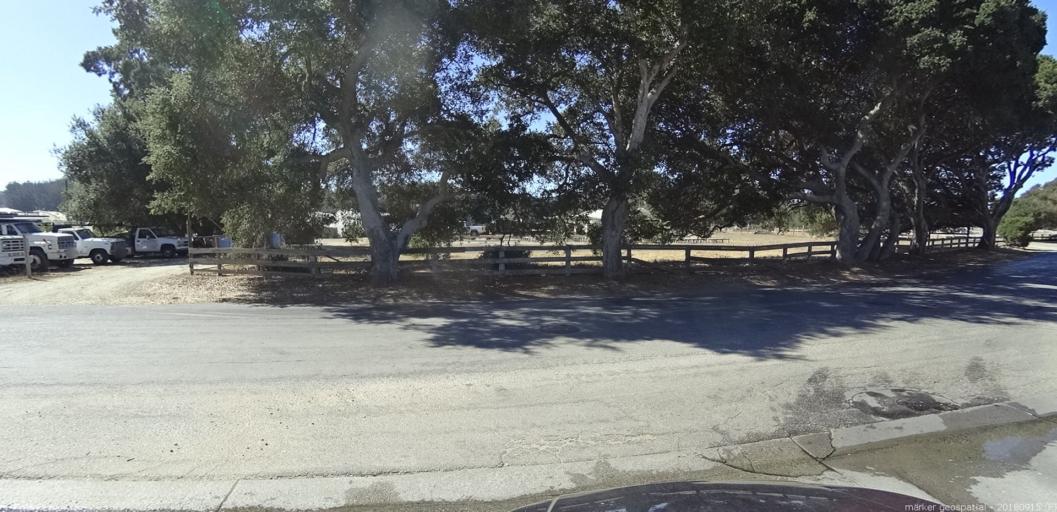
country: US
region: California
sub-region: Monterey County
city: Las Lomas
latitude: 36.8672
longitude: -121.7272
